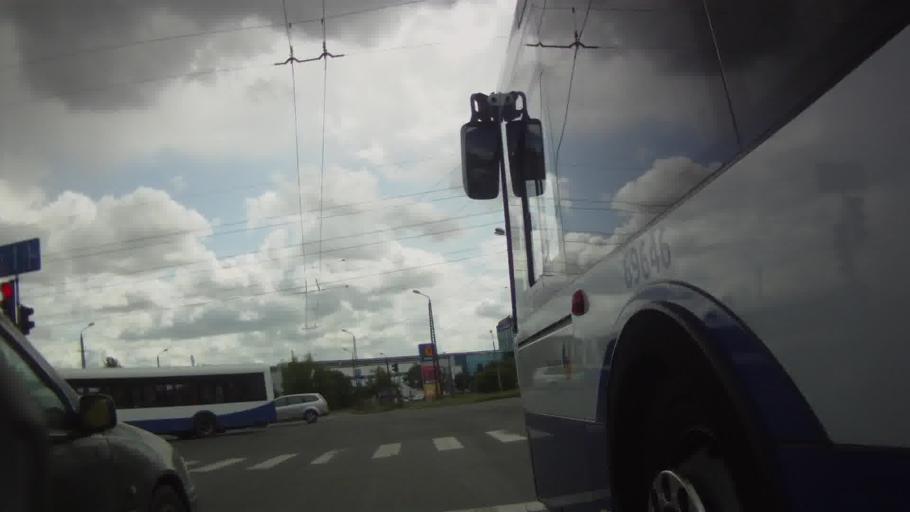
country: LV
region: Stopini
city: Ulbroka
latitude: 56.9324
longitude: 24.2012
